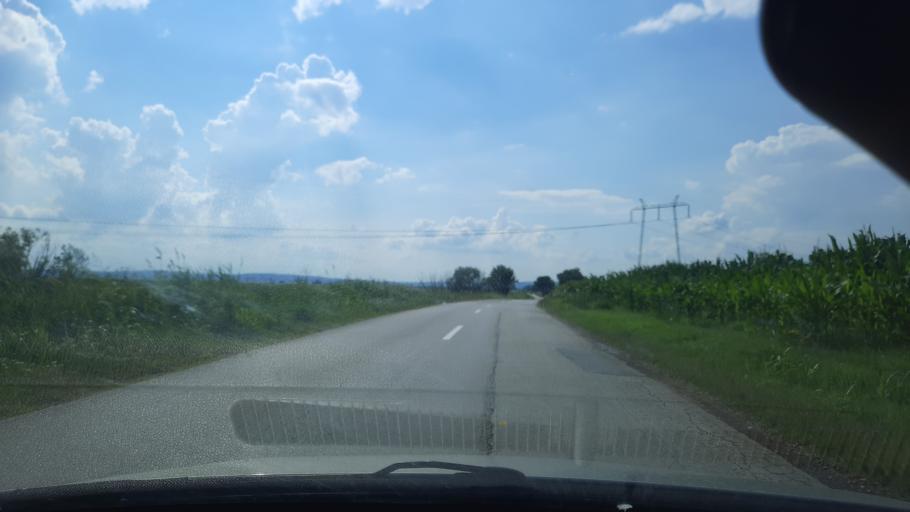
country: RS
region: Central Serbia
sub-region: Branicevski Okrug
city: Malo Crnice
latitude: 44.5779
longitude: 21.3336
